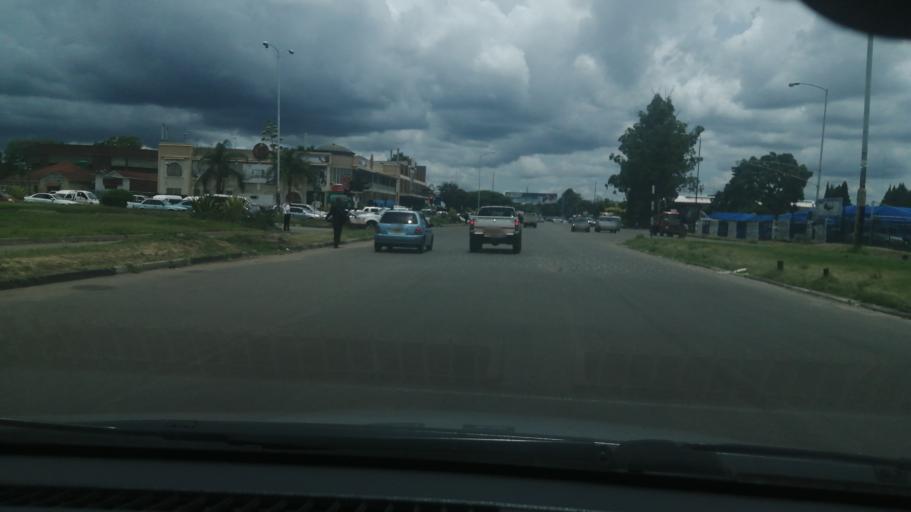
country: ZW
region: Harare
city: Harare
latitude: -17.8300
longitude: 31.0607
